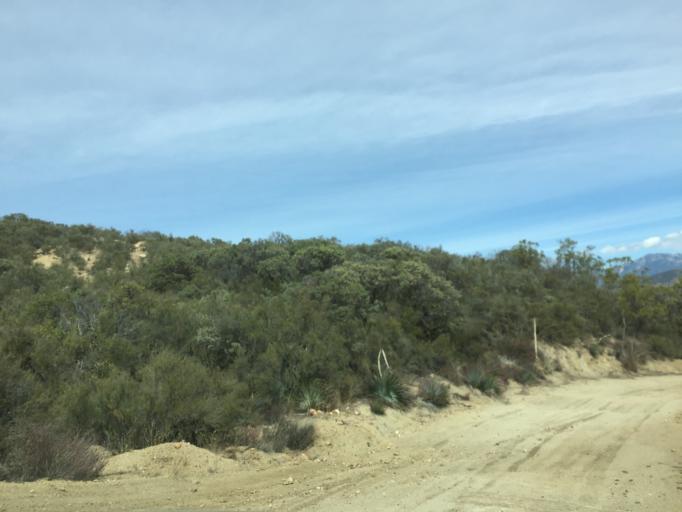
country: US
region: California
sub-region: Riverside County
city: Valle Vista
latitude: 33.6368
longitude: -116.8391
